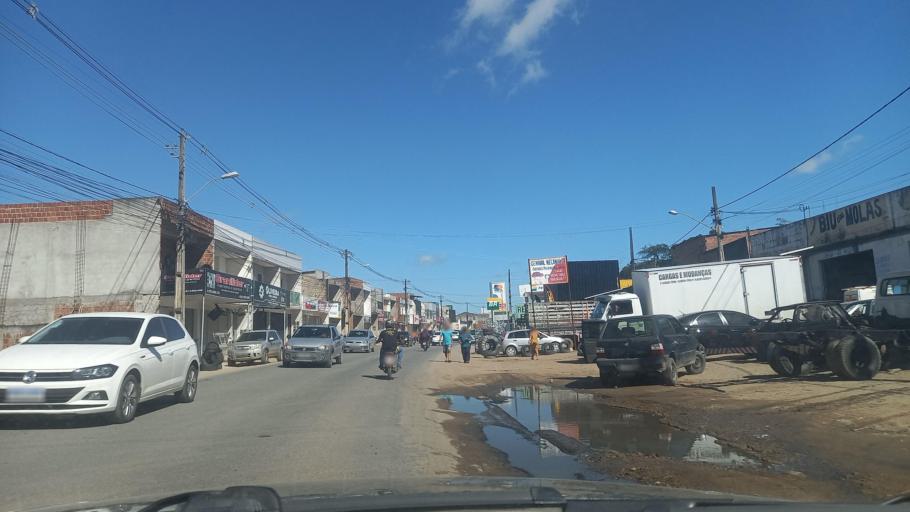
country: BR
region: Pernambuco
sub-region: Vitoria De Santo Antao
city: Vitoria de Santo Antao
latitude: -8.1178
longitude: -35.2990
